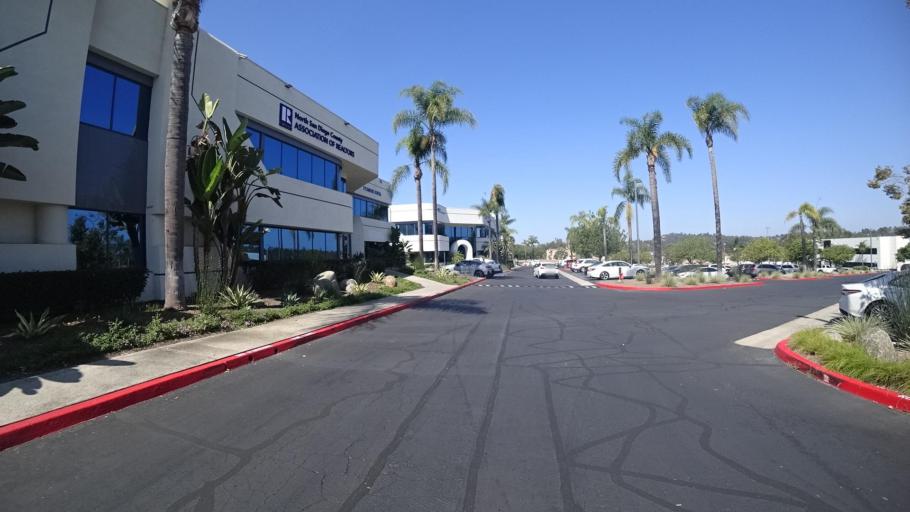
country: US
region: California
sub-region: San Diego County
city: Lake San Marcos
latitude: 33.1593
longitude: -117.2192
